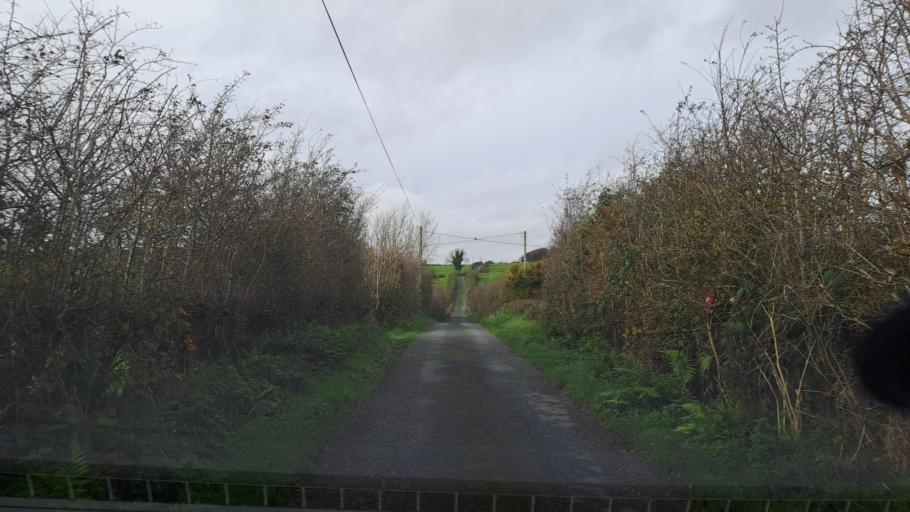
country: IE
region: Ulster
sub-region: County Monaghan
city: Carrickmacross
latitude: 54.0138
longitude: -6.8064
